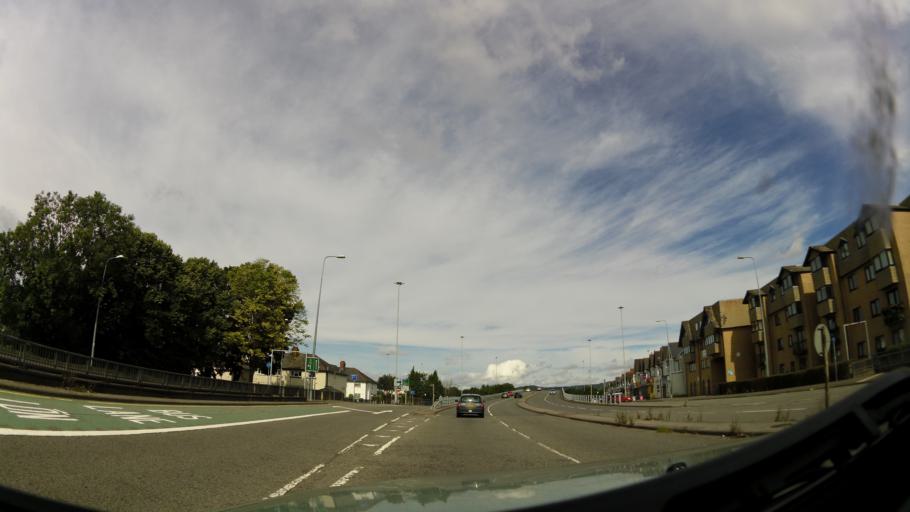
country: GB
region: Wales
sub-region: Cardiff
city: Cardiff
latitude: 51.5023
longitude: -3.1972
